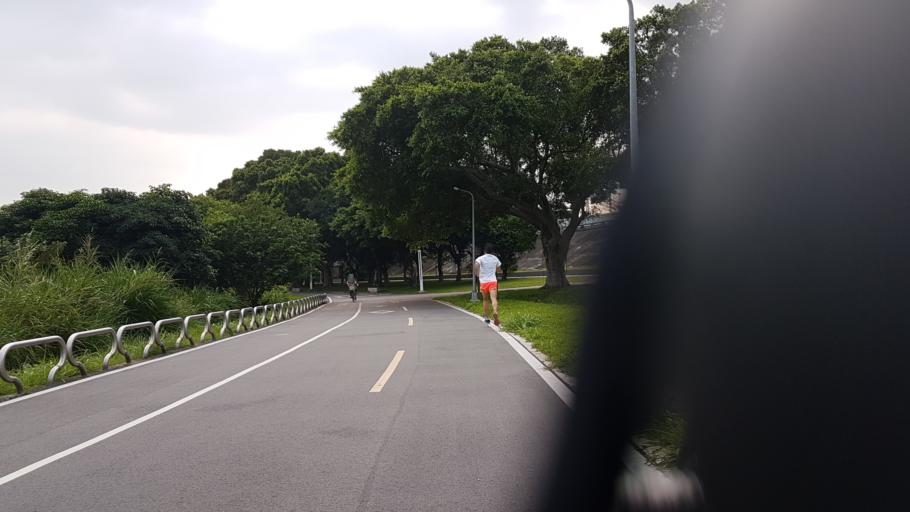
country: TW
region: Taipei
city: Taipei
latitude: 25.0226
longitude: 121.5099
